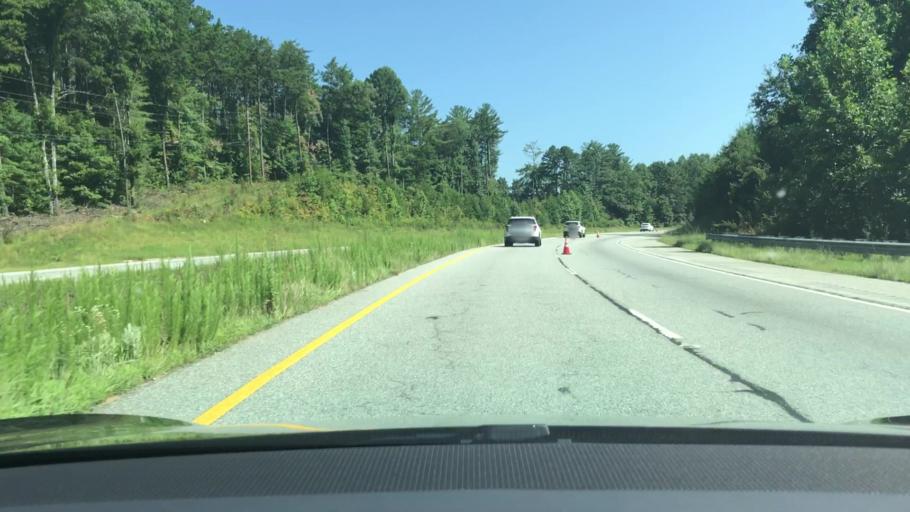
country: US
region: Georgia
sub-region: Rabun County
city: Clayton
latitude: 34.7469
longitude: -83.4017
